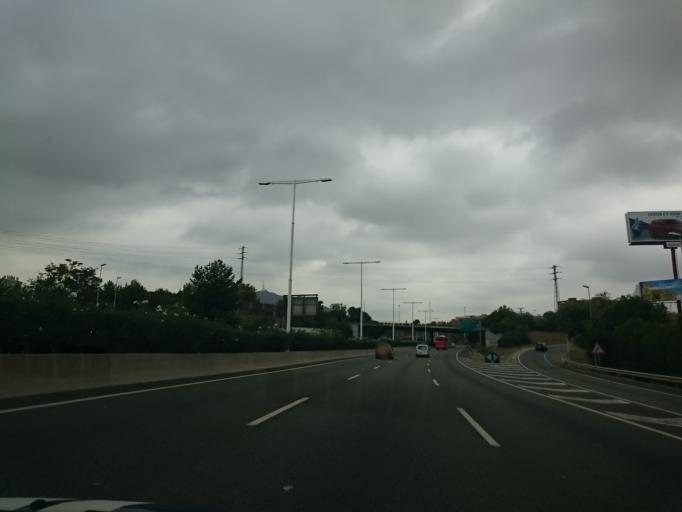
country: ES
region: Catalonia
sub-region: Provincia de Barcelona
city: Esplugues de Llobregat
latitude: 41.3688
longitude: 2.0913
